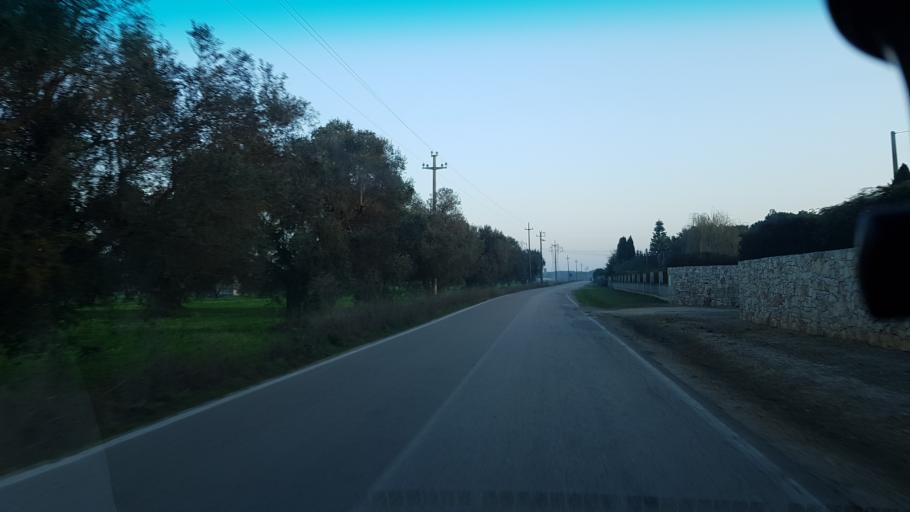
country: IT
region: Apulia
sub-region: Provincia di Brindisi
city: Mesagne
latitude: 40.5893
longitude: 17.7979
